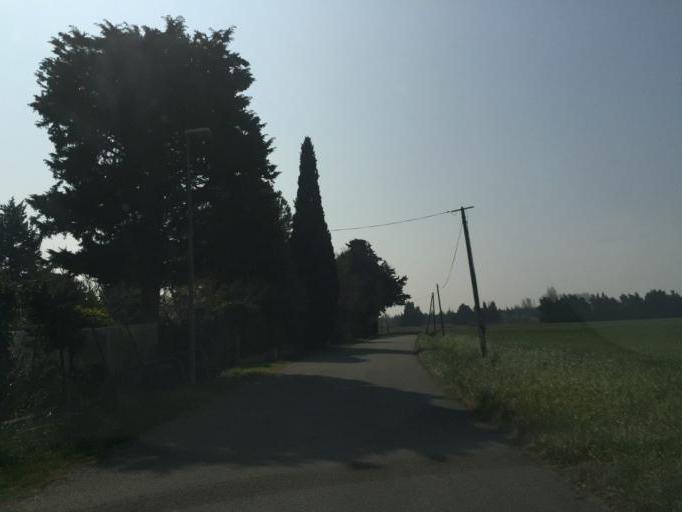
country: FR
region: Provence-Alpes-Cote d'Azur
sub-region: Departement du Vaucluse
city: Jonquieres
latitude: 44.1102
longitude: 4.8988
